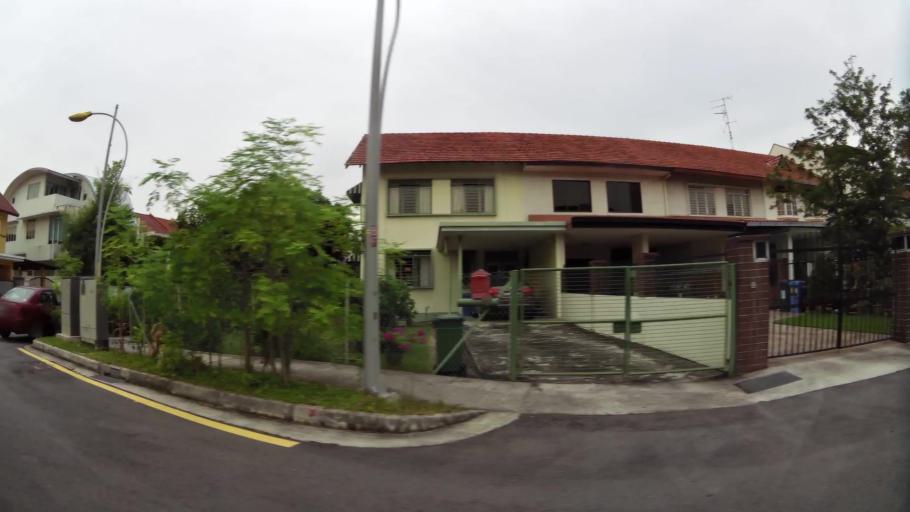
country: SG
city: Singapore
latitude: 1.3312
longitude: 103.8738
